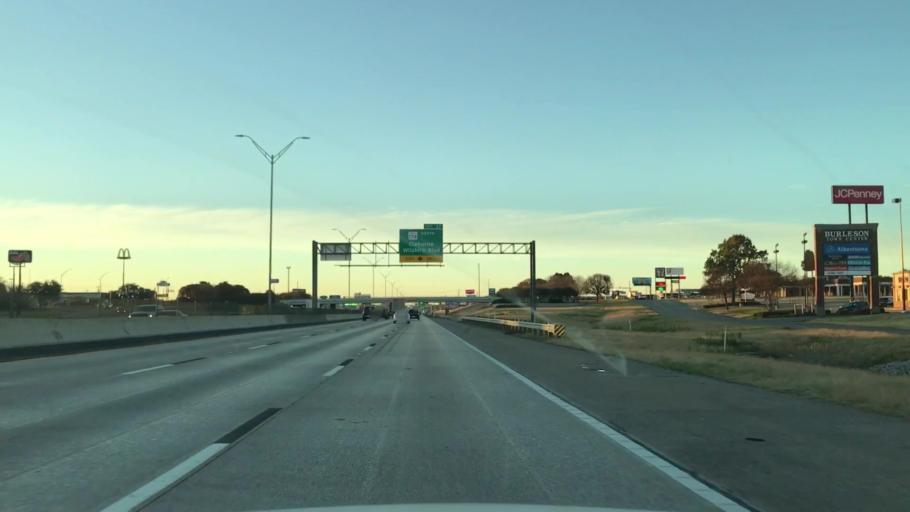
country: US
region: Texas
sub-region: Johnson County
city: Burleson
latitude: 32.5663
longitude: -97.3190
